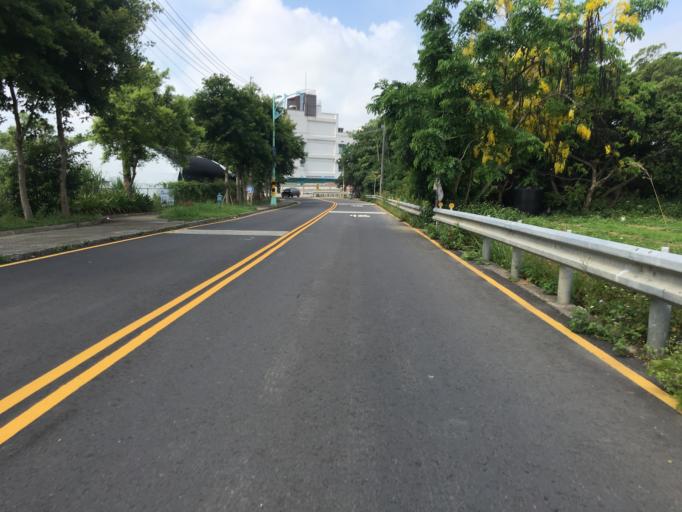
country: TW
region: Taiwan
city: Daxi
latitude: 24.8459
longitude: 121.2425
